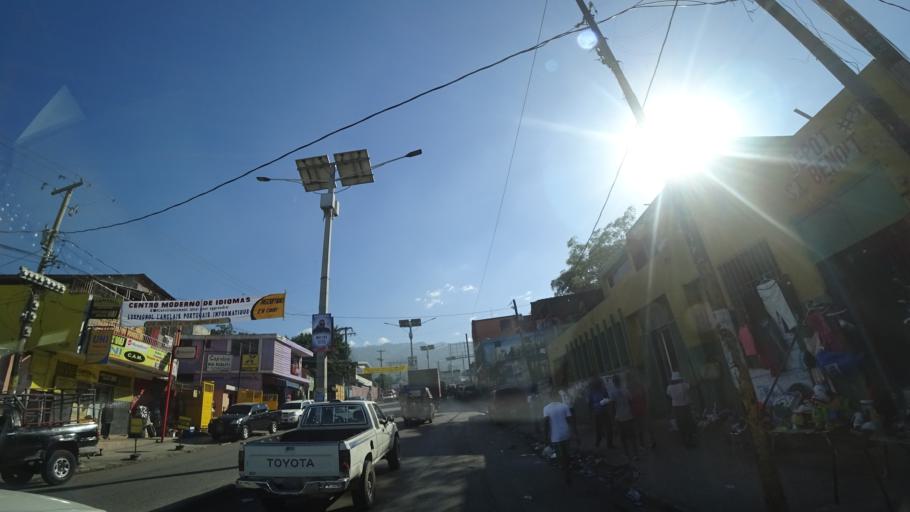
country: HT
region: Ouest
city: Petionville
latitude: 18.5174
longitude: -72.2835
